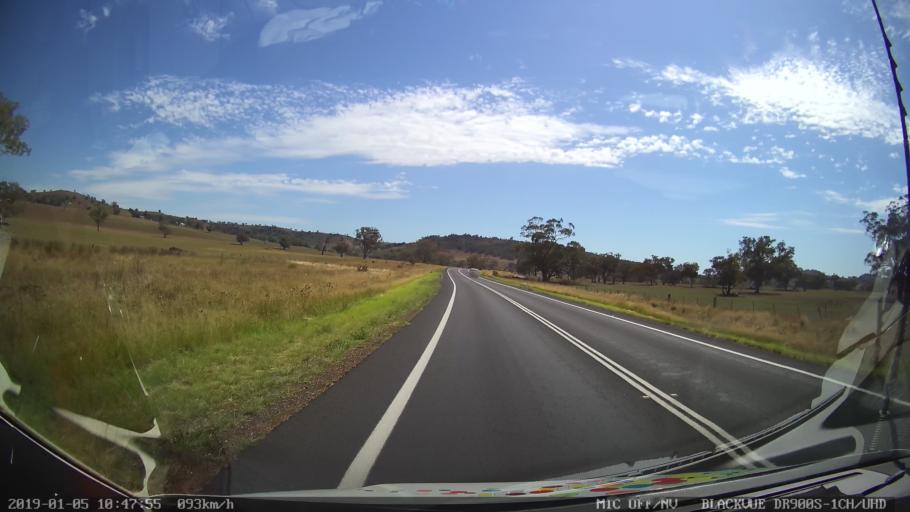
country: AU
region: New South Wales
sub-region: Warrumbungle Shire
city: Coonabarabran
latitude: -31.4407
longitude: 149.0393
